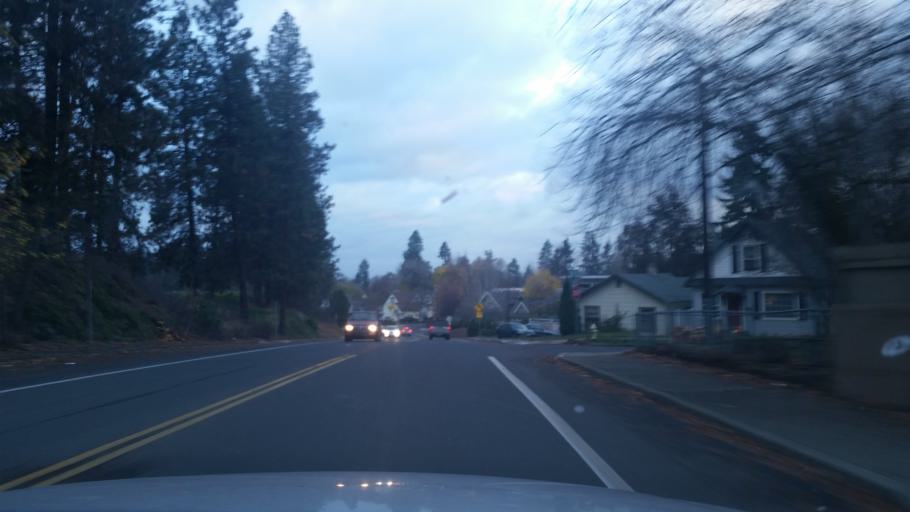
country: US
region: Washington
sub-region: Spokane County
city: Spokane
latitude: 47.6447
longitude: -117.3988
